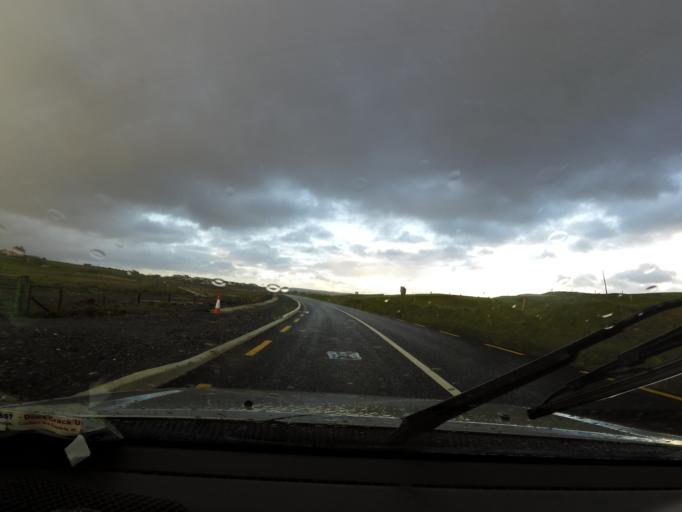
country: IE
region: Munster
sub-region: An Clar
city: Kilrush
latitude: 52.9444
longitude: -9.3645
